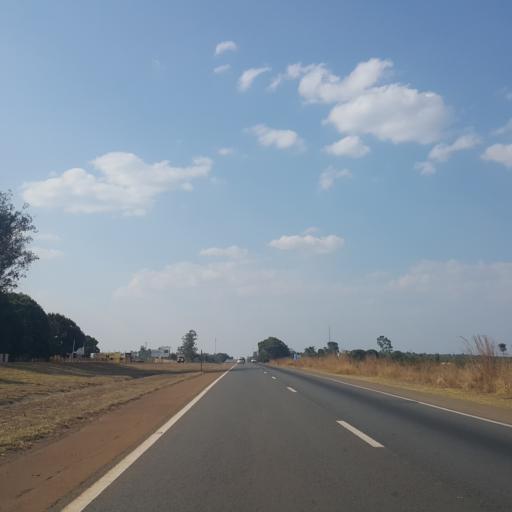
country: BR
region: Goias
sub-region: Abadiania
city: Abadiania
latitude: -16.2380
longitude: -48.7597
